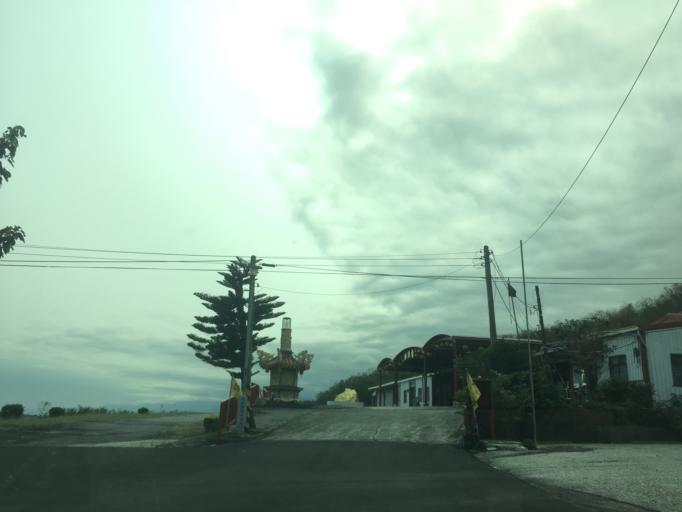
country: TW
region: Taiwan
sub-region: Taitung
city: Taitung
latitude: 22.7906
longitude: 121.1601
